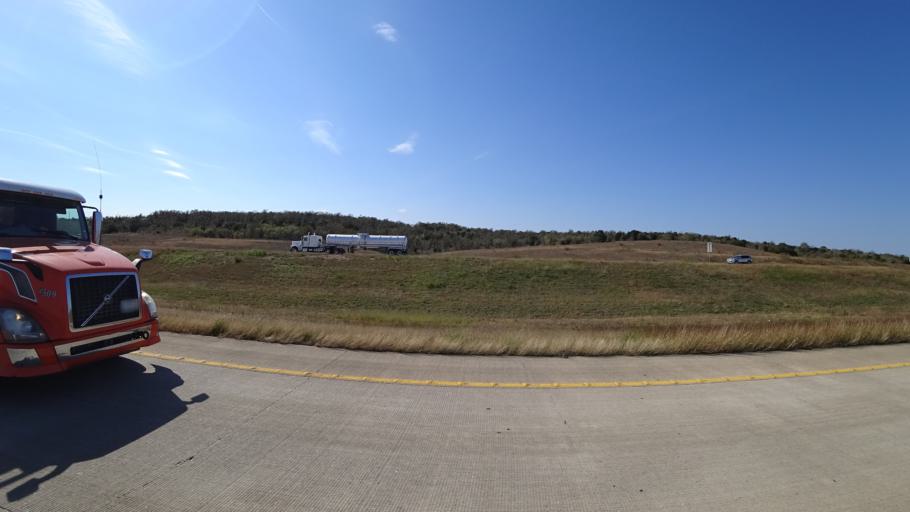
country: US
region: Texas
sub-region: Travis County
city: Manor
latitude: 30.3139
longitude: -97.5721
